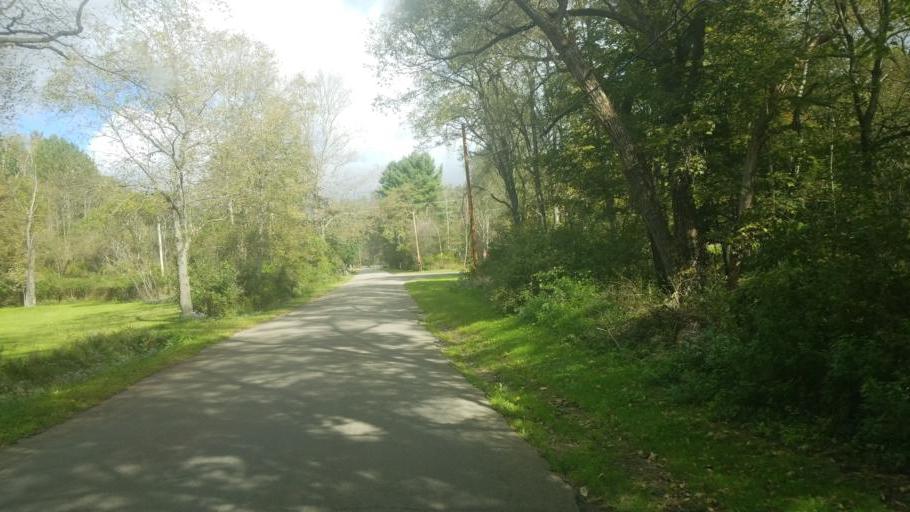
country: US
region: New York
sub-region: Cattaraugus County
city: Weston Mills
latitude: 42.1420
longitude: -78.3500
